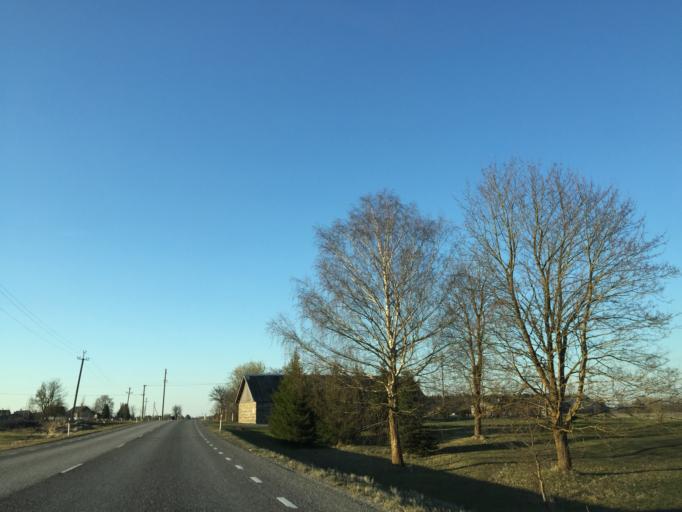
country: EE
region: Ida-Virumaa
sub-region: Johvi vald
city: Johvi
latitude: 59.2991
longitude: 27.4952
